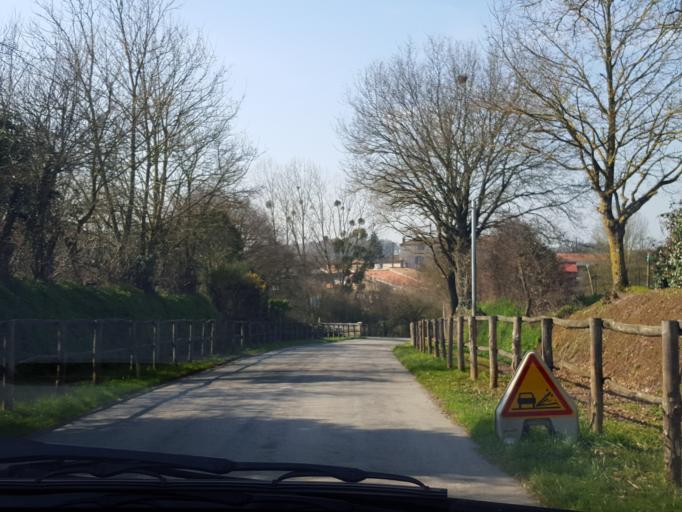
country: FR
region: Pays de la Loire
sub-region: Departement de la Vendee
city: Vendrennes
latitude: 46.8305
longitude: -1.1531
